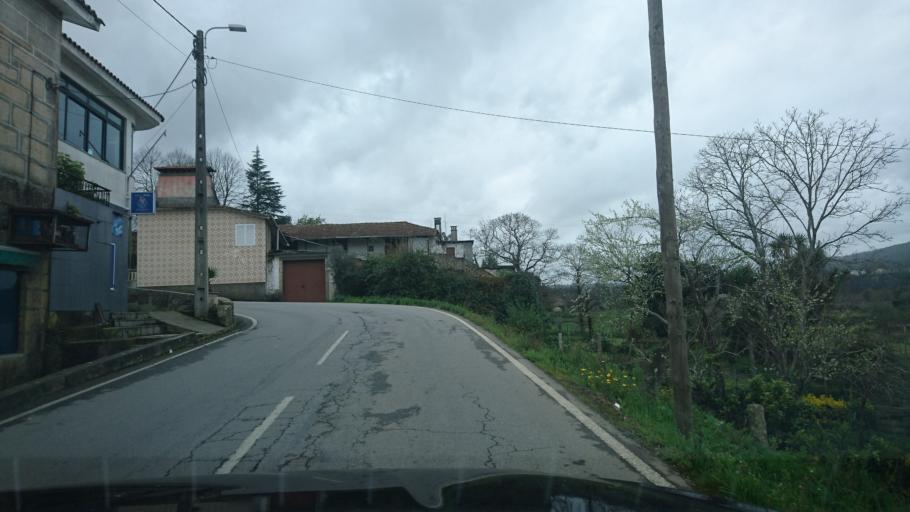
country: PT
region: Porto
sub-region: Paredes
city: Recarei
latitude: 41.1413
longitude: -8.3930
